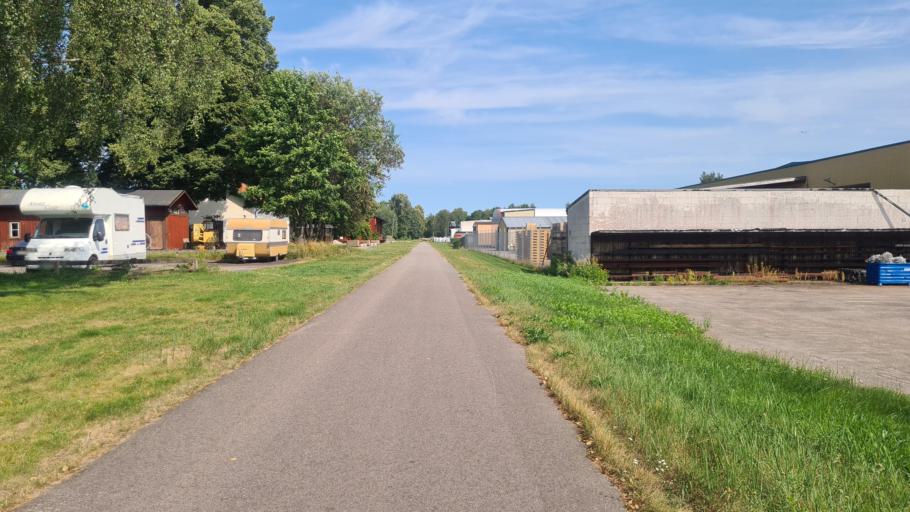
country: SE
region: Kronoberg
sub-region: Ljungby Kommun
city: Lagan
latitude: 56.9129
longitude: 13.9897
